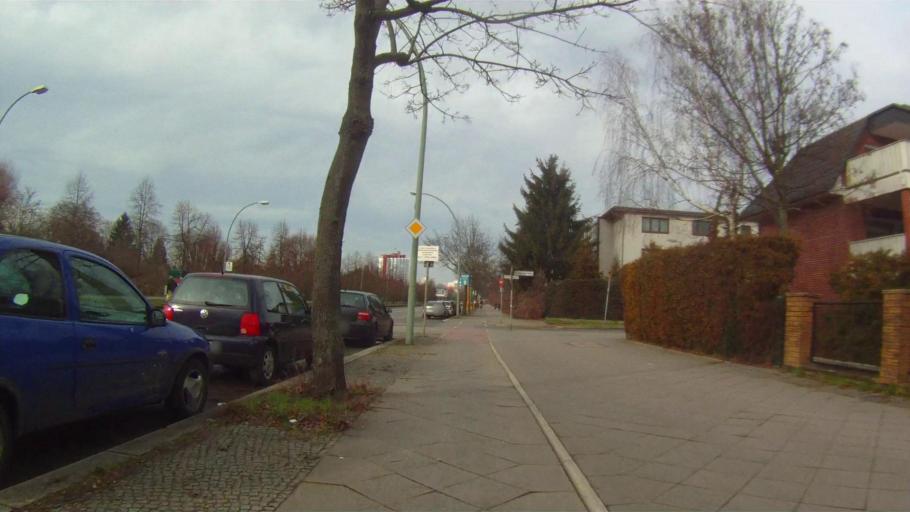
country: DE
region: Berlin
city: Rudow
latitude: 52.4172
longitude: 13.4941
